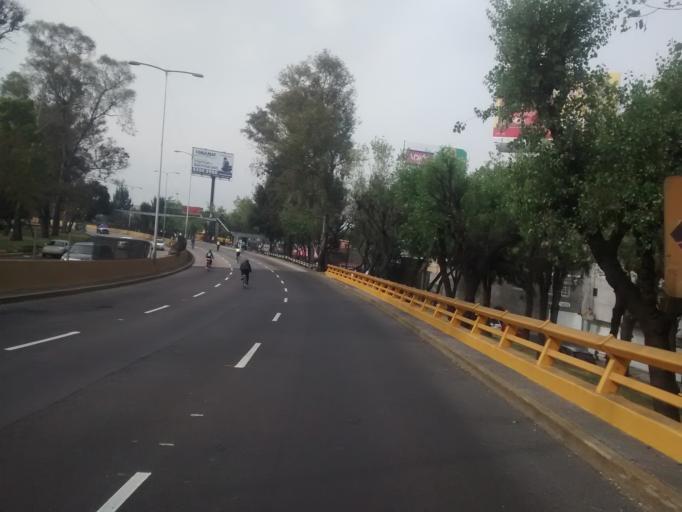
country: MX
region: Mexico City
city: Colonia Nativitas
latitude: 19.3693
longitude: -99.1238
